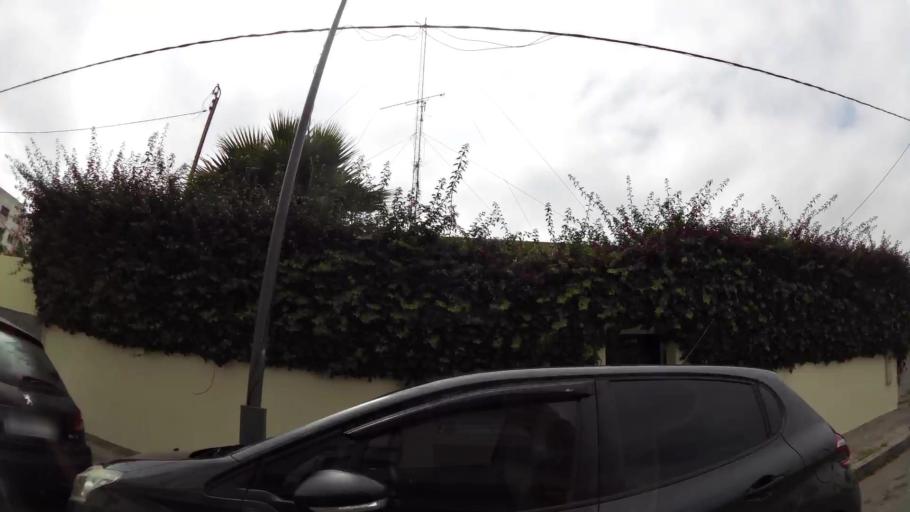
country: MA
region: Rabat-Sale-Zemmour-Zaer
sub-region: Rabat
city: Rabat
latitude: 34.0136
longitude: -6.8532
